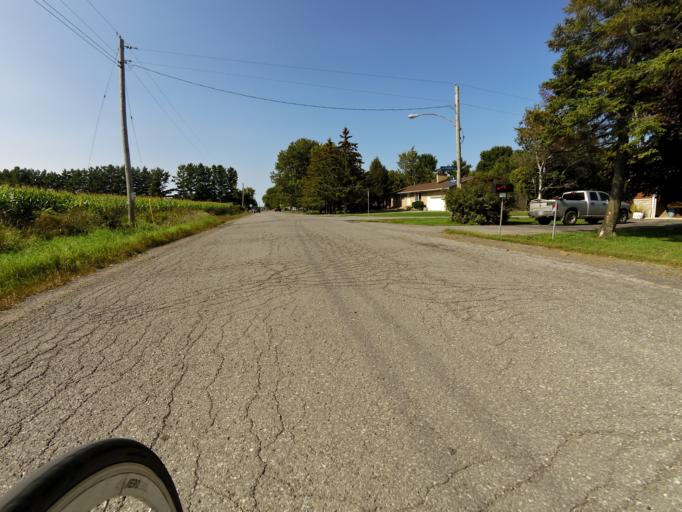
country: CA
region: Ontario
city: Carleton Place
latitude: 45.3582
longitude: -76.1224
